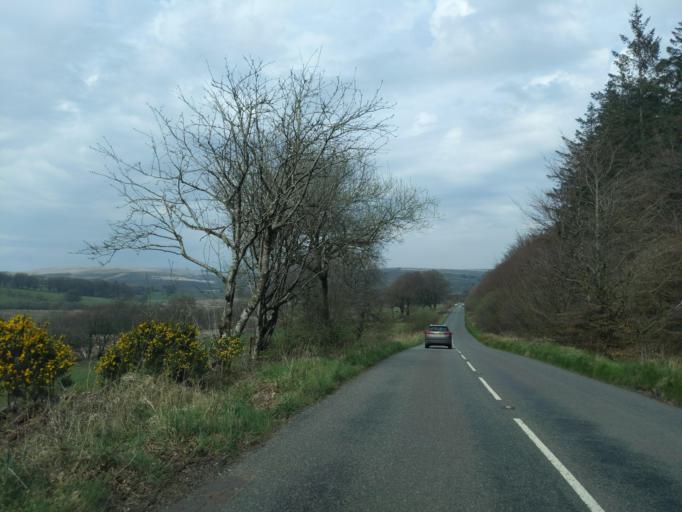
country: GB
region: England
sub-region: Devon
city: Okehampton
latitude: 50.5890
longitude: -3.9197
